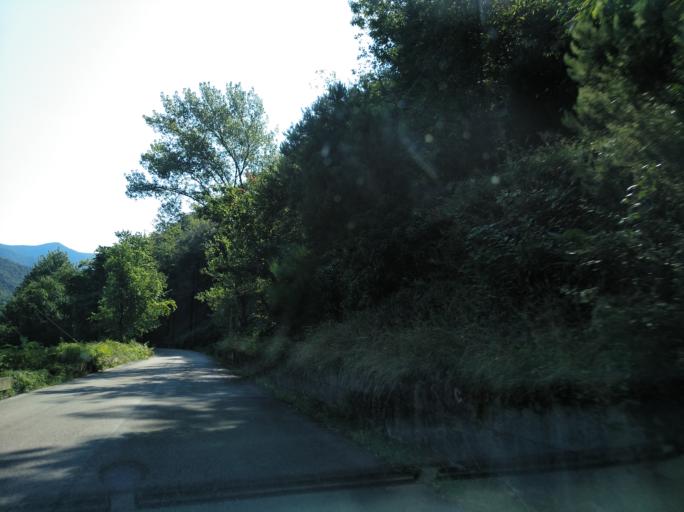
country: ES
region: Catalonia
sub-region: Provincia de Girona
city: Susqueda
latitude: 41.9823
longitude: 2.5307
